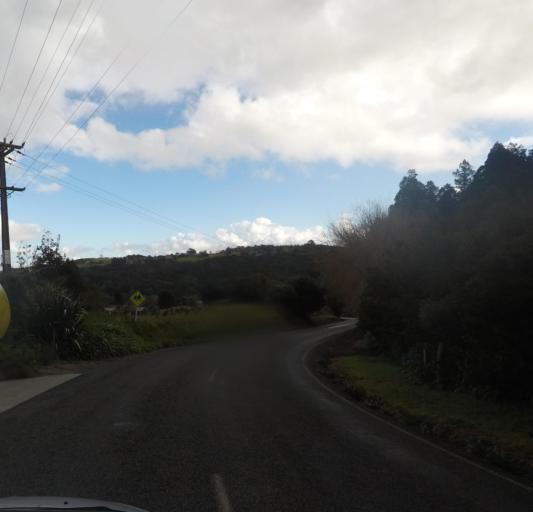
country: NZ
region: Auckland
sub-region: Auckland
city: Warkworth
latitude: -36.3792
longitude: 174.7590
